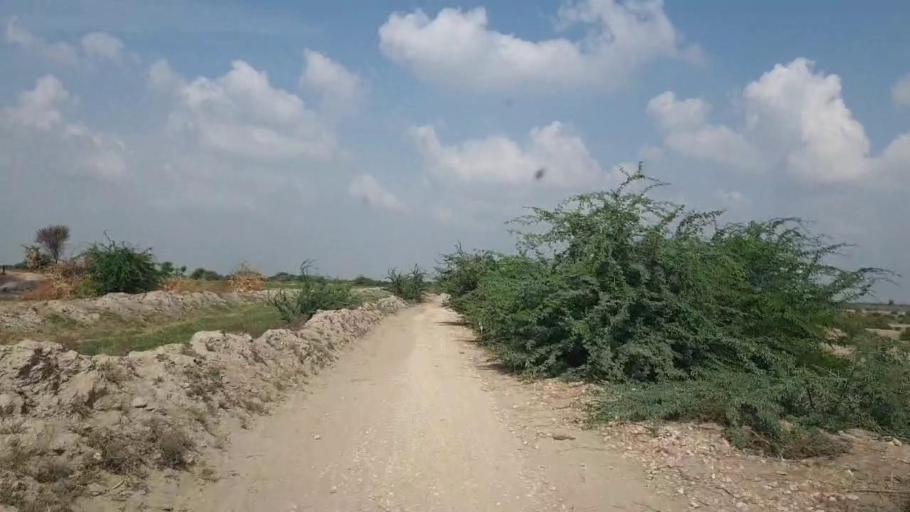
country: PK
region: Sindh
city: Badin
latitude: 24.4998
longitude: 68.6557
